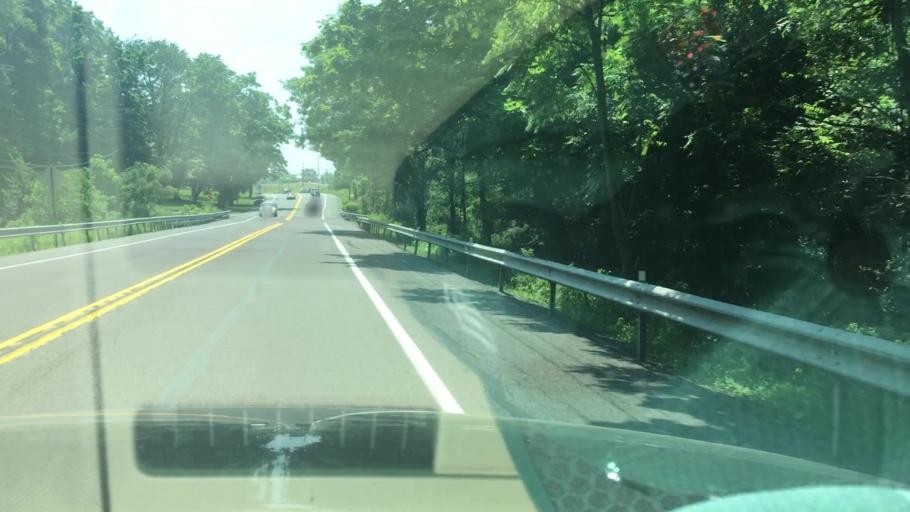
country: US
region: Pennsylvania
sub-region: Lehigh County
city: Trexlertown
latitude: 40.5982
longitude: -75.6316
